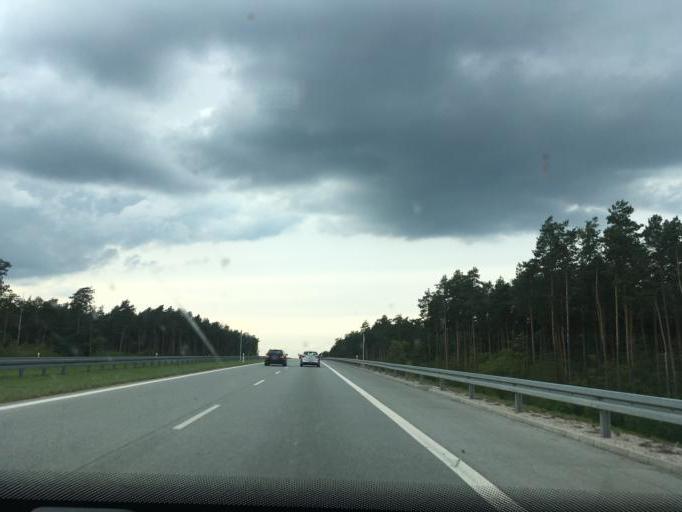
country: PL
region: Lodz Voivodeship
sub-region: Powiat zdunskowolski
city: Zdunska Wola
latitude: 51.5723
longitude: 18.9575
